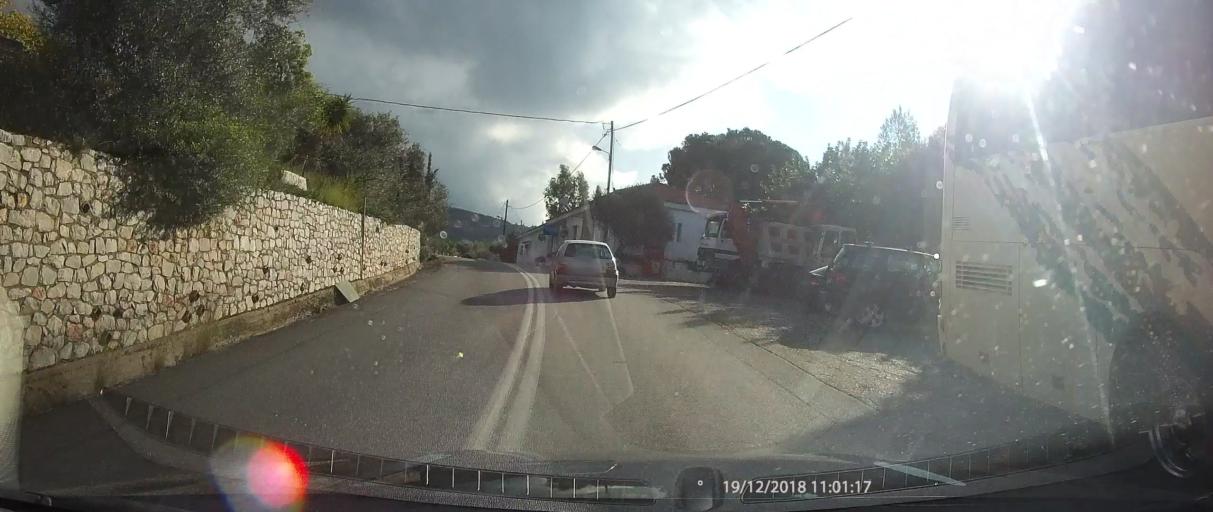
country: GR
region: Peloponnese
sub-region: Nomos Messinias
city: Kardamyli
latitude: 36.8857
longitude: 22.2342
